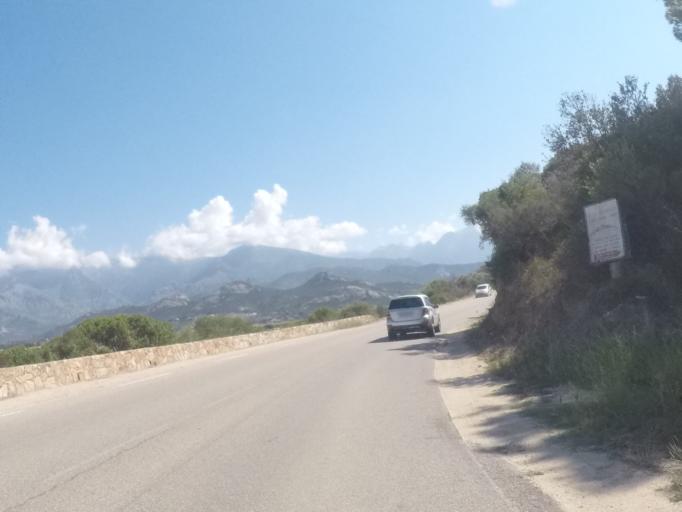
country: FR
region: Corsica
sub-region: Departement de la Haute-Corse
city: Calvi
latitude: 42.5428
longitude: 8.7899
